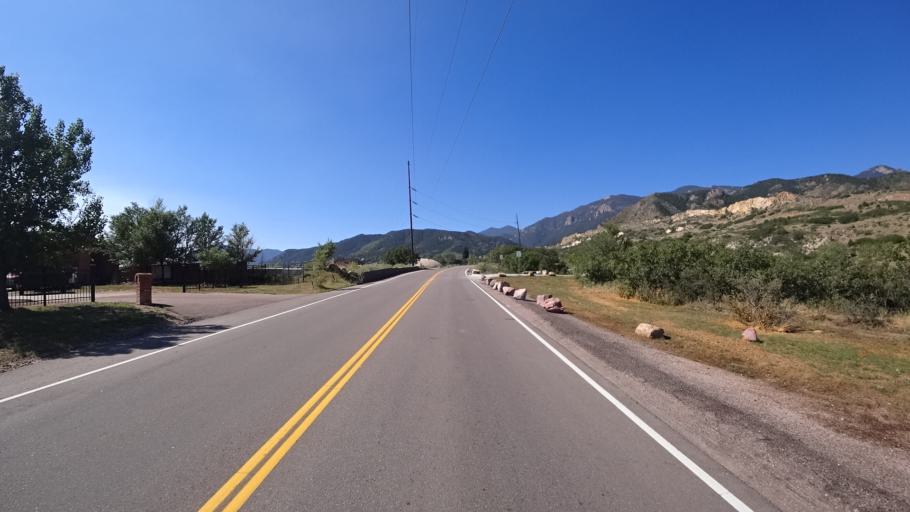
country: US
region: Colorado
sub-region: El Paso County
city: Manitou Springs
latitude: 38.8344
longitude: -104.8765
